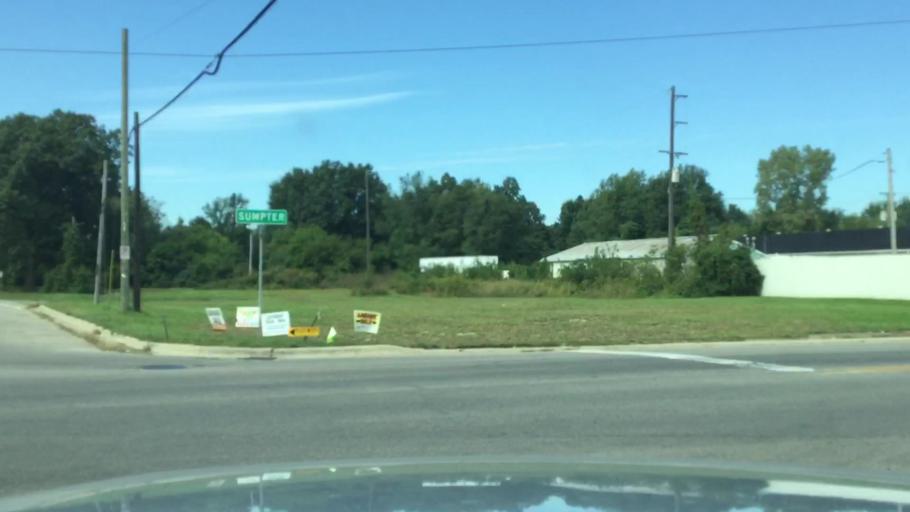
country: US
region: Michigan
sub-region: Wayne County
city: Belleville
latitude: 42.1607
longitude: -83.4823
